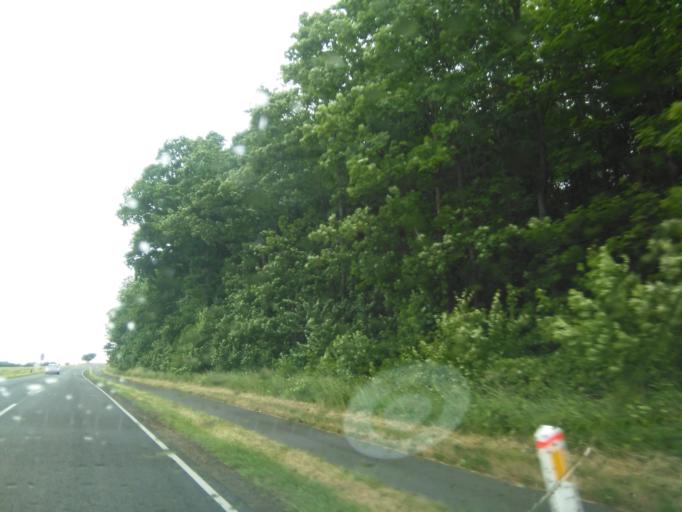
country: DK
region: Capital Region
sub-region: Bornholm Kommune
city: Akirkeby
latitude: 55.0472
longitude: 14.8317
